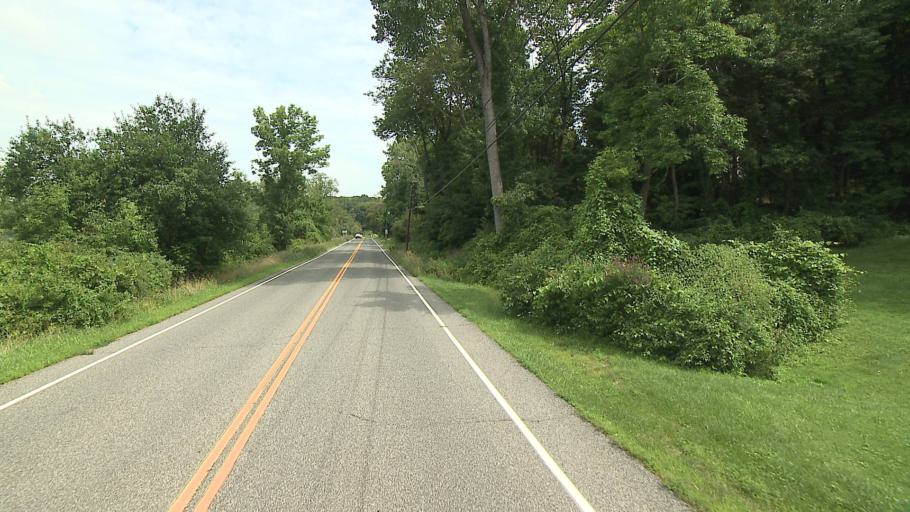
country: US
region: Connecticut
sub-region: Fairfield County
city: Sherman
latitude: 41.6353
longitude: -73.4997
